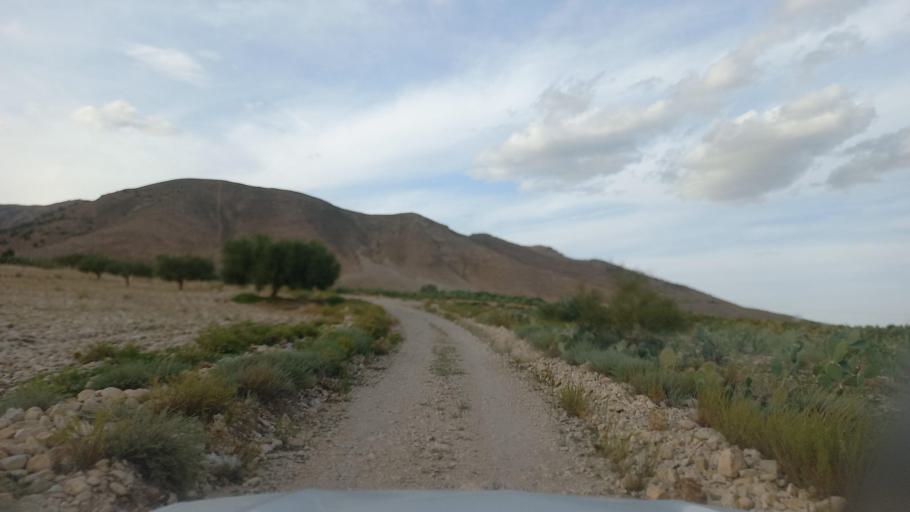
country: TN
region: Al Qasrayn
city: Sbiba
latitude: 35.4490
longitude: 9.0662
